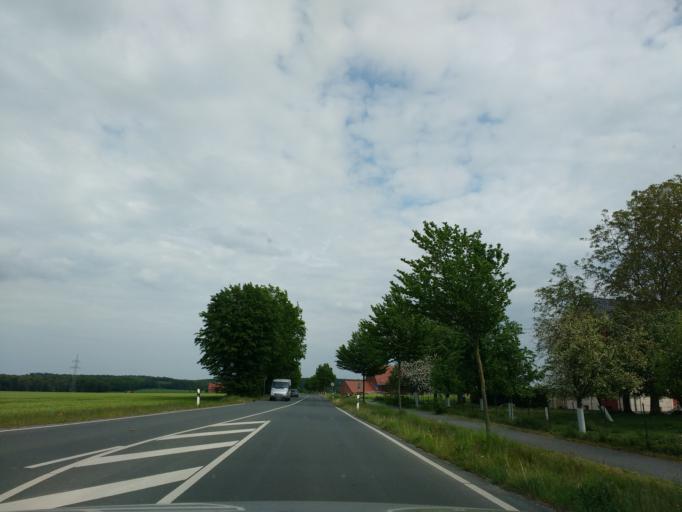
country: DE
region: North Rhine-Westphalia
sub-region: Regierungsbezirk Detmold
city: Salzkotten
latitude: 51.6688
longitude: 8.6276
